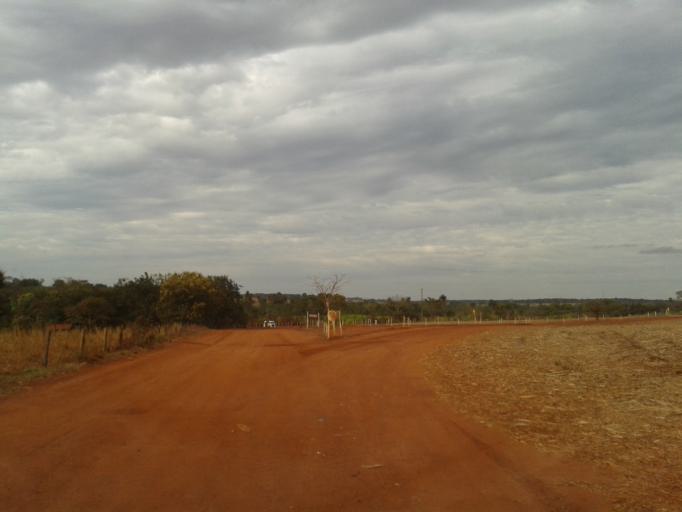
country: BR
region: Minas Gerais
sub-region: Santa Vitoria
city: Santa Vitoria
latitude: -18.7877
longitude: -50.1821
